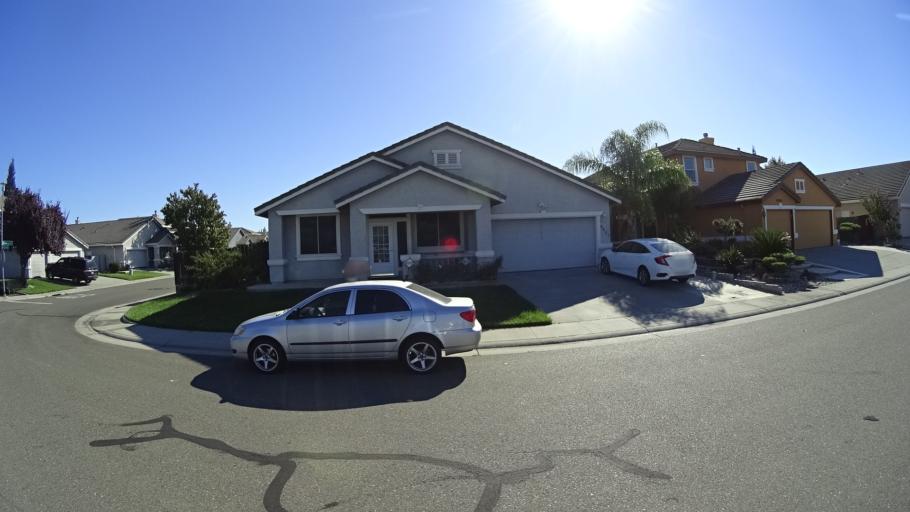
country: US
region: California
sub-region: Sacramento County
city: Vineyard
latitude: 38.4496
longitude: -121.3780
